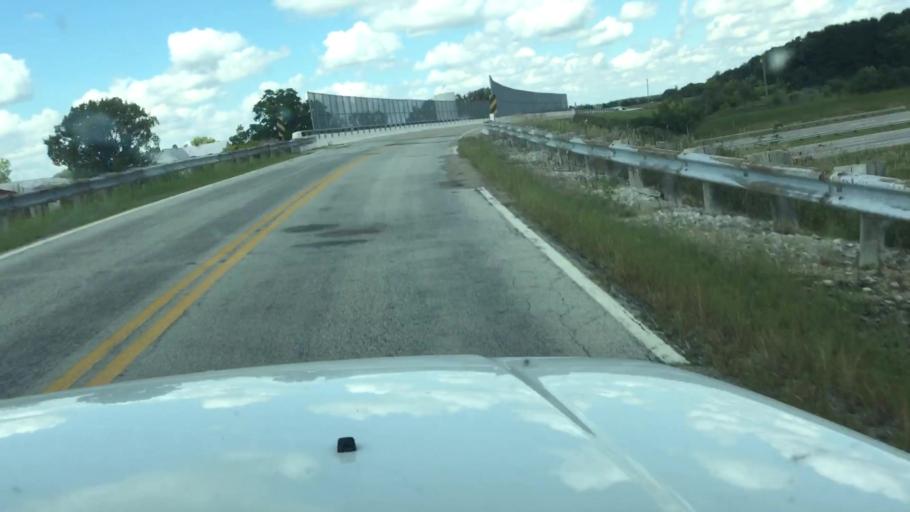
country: US
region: Ohio
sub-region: Madison County
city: Choctaw Lake
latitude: 39.9370
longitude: -83.5699
